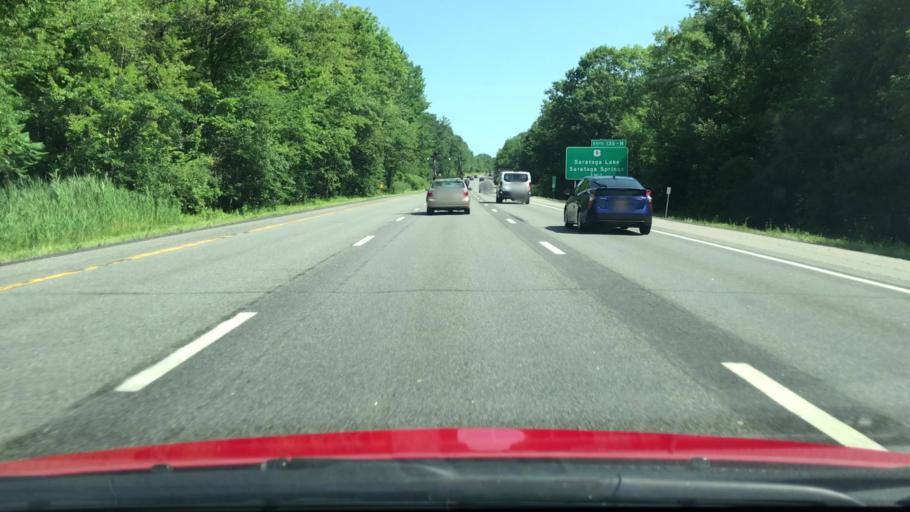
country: US
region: New York
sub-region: Saratoga County
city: Ballston Spa
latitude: 43.0012
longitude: -73.8025
